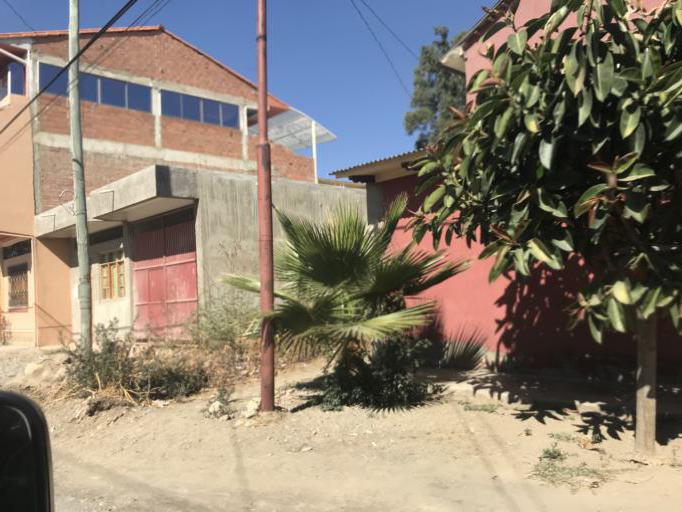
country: BO
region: Cochabamba
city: Punata
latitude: -17.5569
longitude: -65.8621
